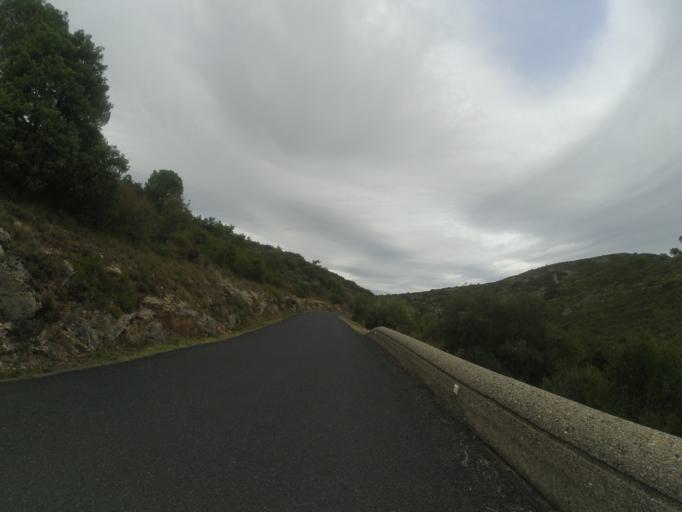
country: FR
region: Languedoc-Roussillon
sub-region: Departement des Pyrenees-Orientales
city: Estagel
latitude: 42.7668
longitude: 2.7036
